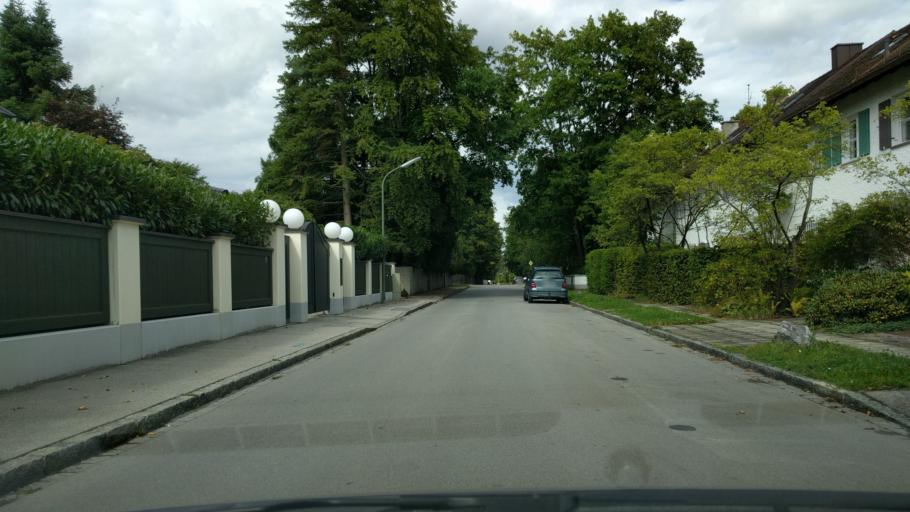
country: DE
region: Bavaria
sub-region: Upper Bavaria
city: Pullach im Isartal
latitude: 48.0574
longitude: 11.5467
